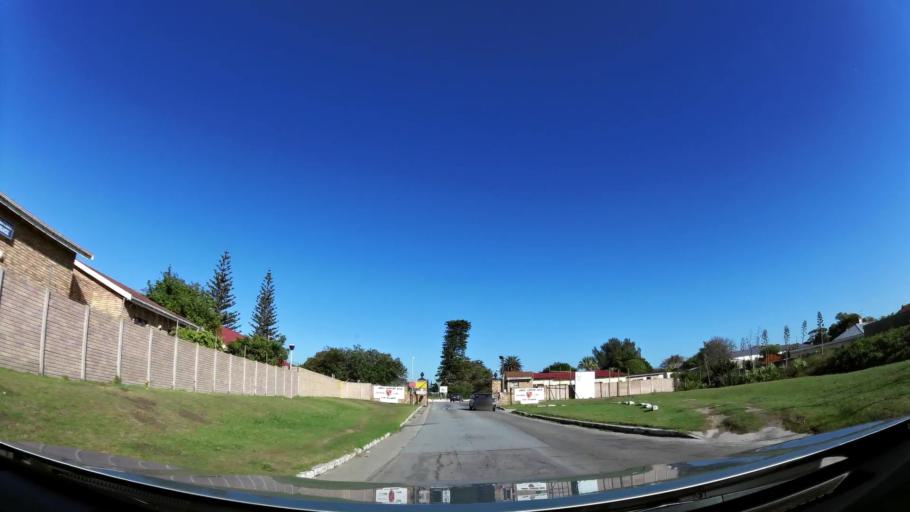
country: ZA
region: Eastern Cape
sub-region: Nelson Mandela Bay Metropolitan Municipality
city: Port Elizabeth
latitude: -33.9825
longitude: 25.6281
